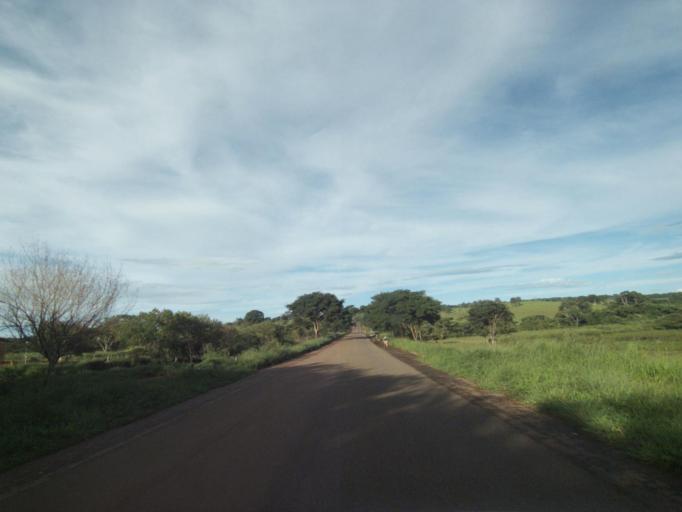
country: BR
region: Goias
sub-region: Itaberai
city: Itaberai
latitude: -15.9172
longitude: -49.5945
